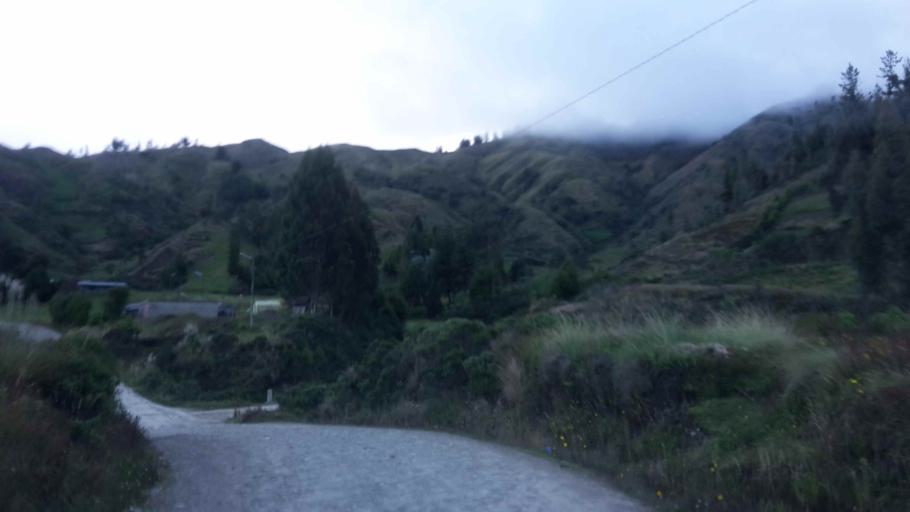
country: BO
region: Cochabamba
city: Colomi
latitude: -17.2465
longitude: -65.9064
